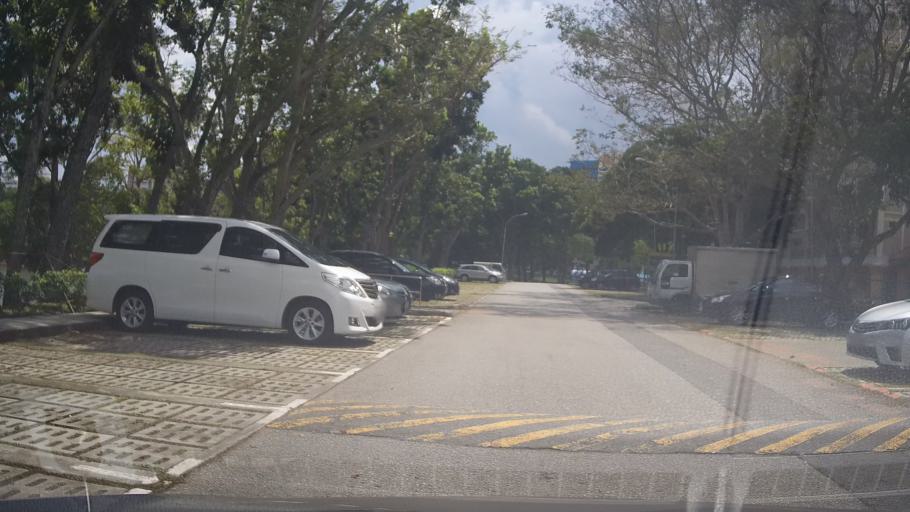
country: MY
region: Johor
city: Kampung Pasir Gudang Baru
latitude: 1.3715
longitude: 103.9511
